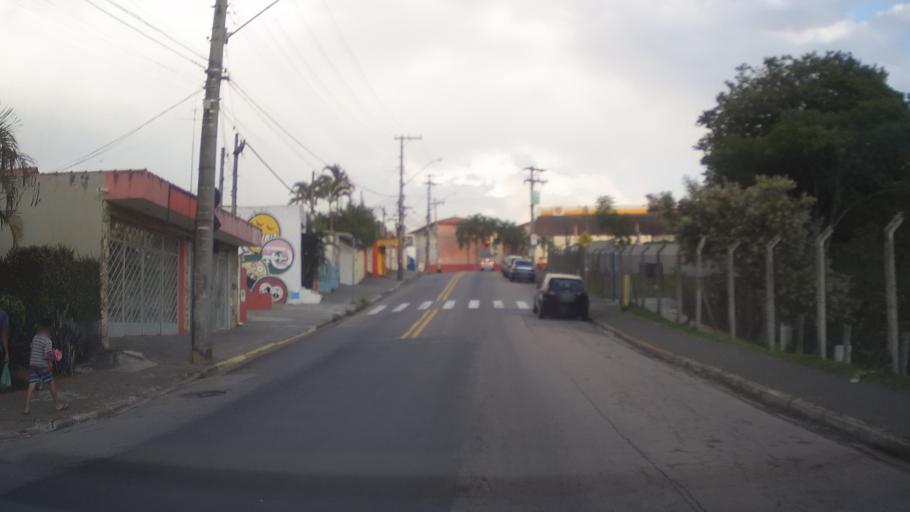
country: BR
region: Sao Paulo
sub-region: Jundiai
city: Jundiai
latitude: -23.1871
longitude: -46.9612
